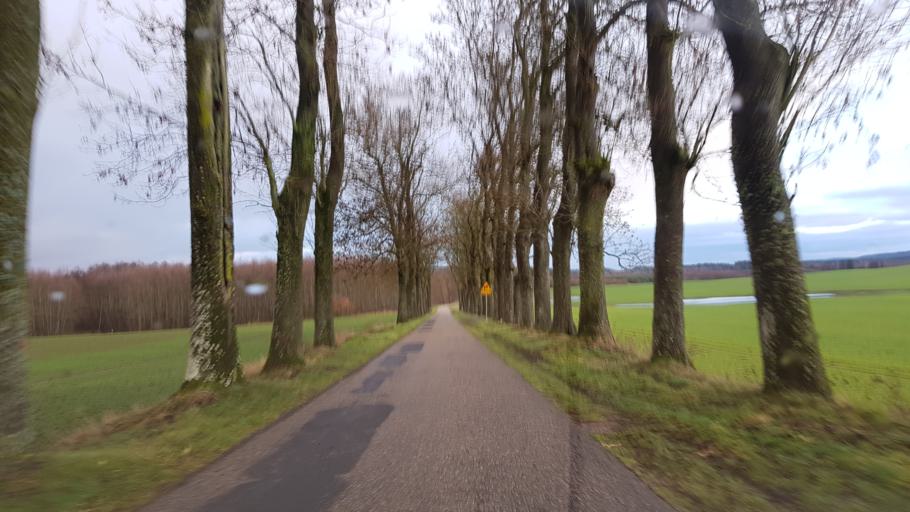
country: PL
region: West Pomeranian Voivodeship
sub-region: Powiat swidwinski
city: Rabino
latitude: 53.9425
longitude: 15.9328
